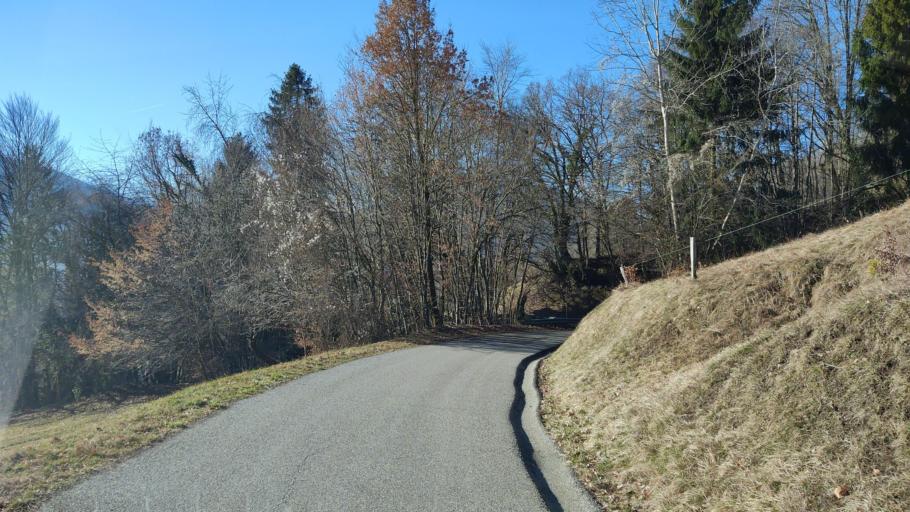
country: FR
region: Rhone-Alpes
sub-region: Departement de la Savoie
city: La Rochette
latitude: 45.4568
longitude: 6.0955
